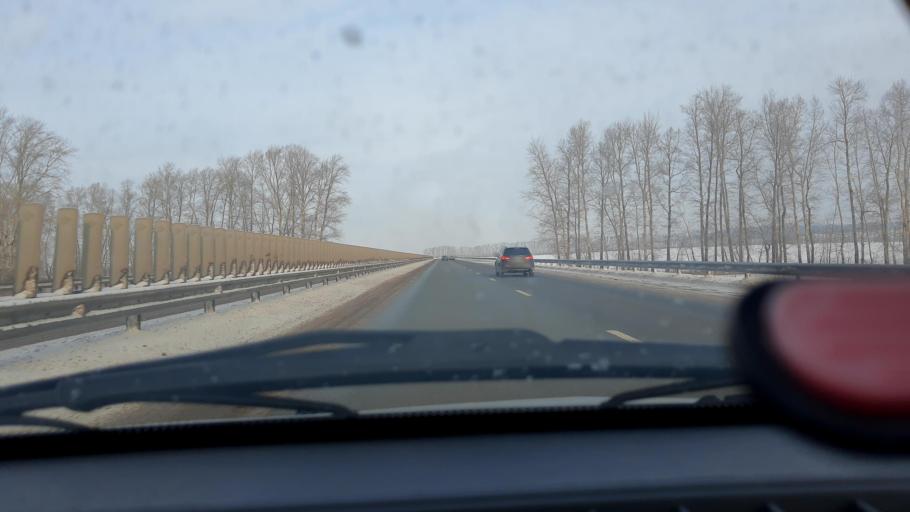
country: RU
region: Bashkortostan
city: Asanovo
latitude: 54.9478
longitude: 55.5833
